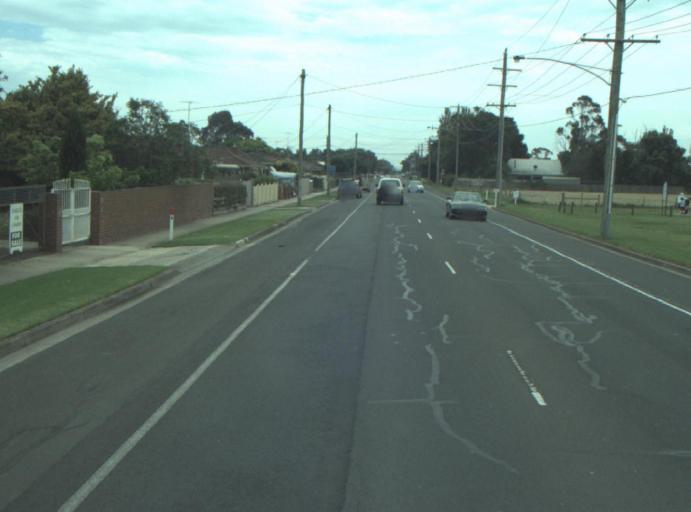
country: AU
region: Victoria
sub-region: Greater Geelong
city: Breakwater
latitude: -38.1780
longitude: 144.4016
